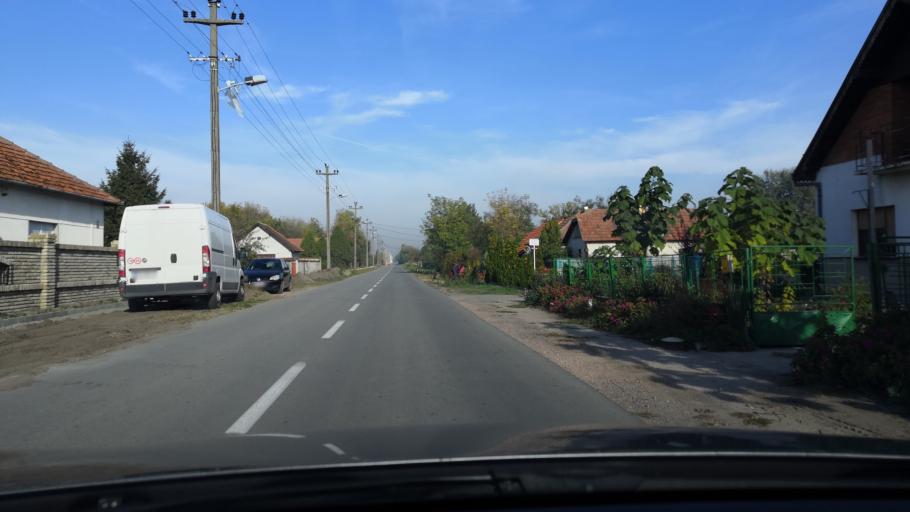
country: HU
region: Csongrad
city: Morahalom
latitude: 46.1308
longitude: 19.8553
